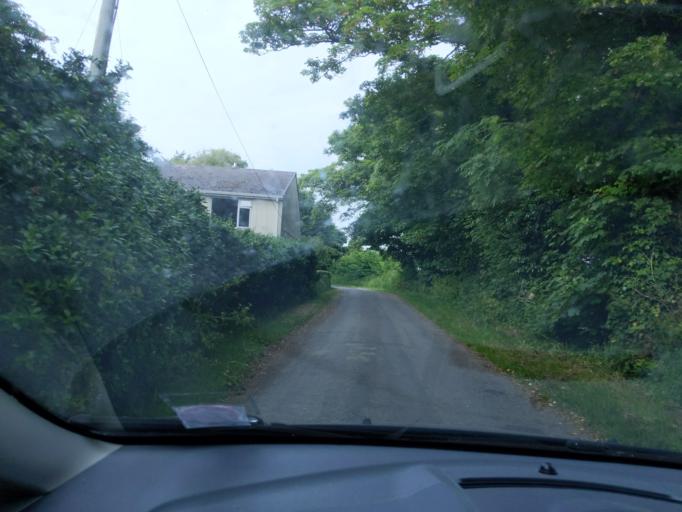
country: IM
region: Ramsey
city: Ramsey
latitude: 54.3562
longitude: -4.4463
